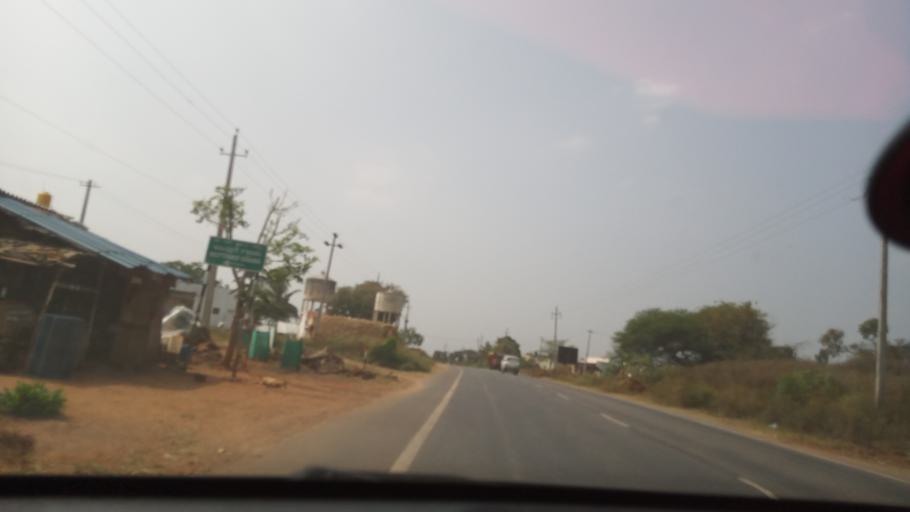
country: IN
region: Karnataka
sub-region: Chamrajnagar
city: Chamrajnagar
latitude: 11.9971
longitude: 76.8511
